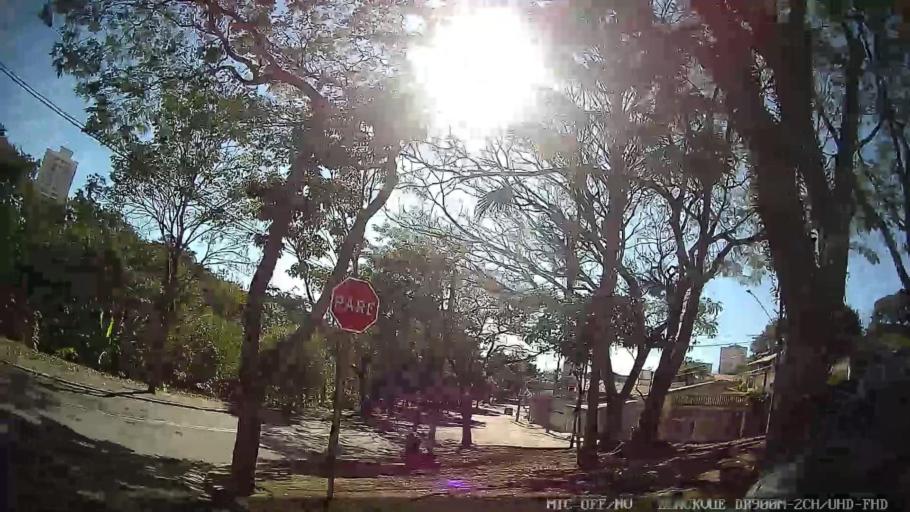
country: BR
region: Sao Paulo
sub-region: Sao Jose Dos Campos
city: Sao Jose dos Campos
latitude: -23.2262
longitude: -45.8944
